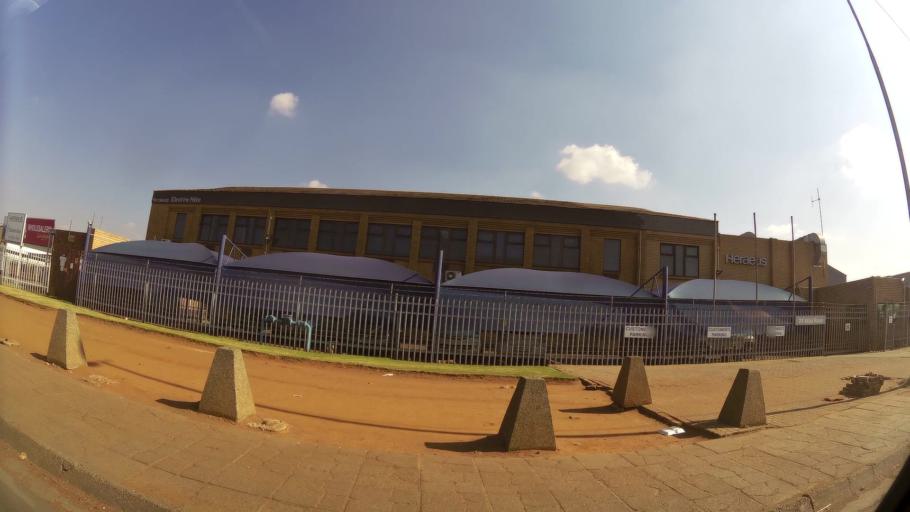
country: ZA
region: Gauteng
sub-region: Ekurhuleni Metropolitan Municipality
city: Boksburg
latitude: -26.2020
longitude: 28.2838
